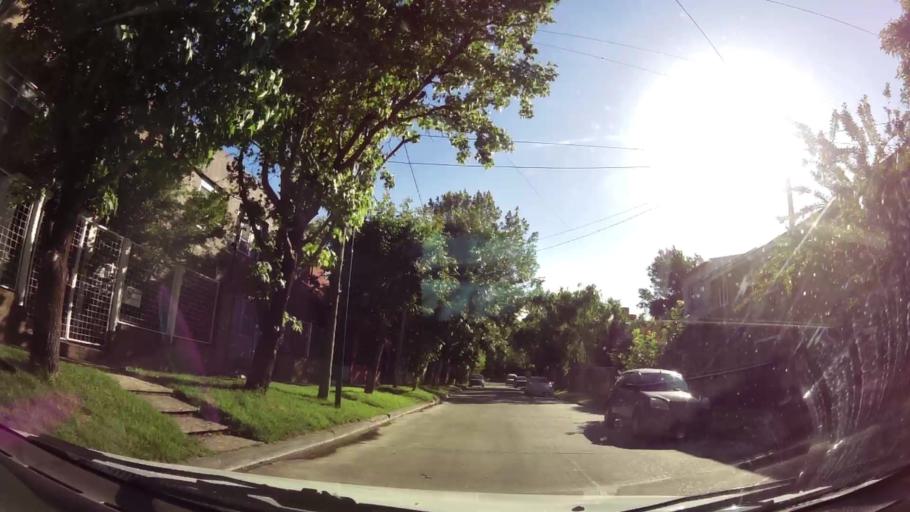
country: AR
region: Buenos Aires
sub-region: Partido de San Isidro
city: San Isidro
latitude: -34.4677
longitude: -58.5026
